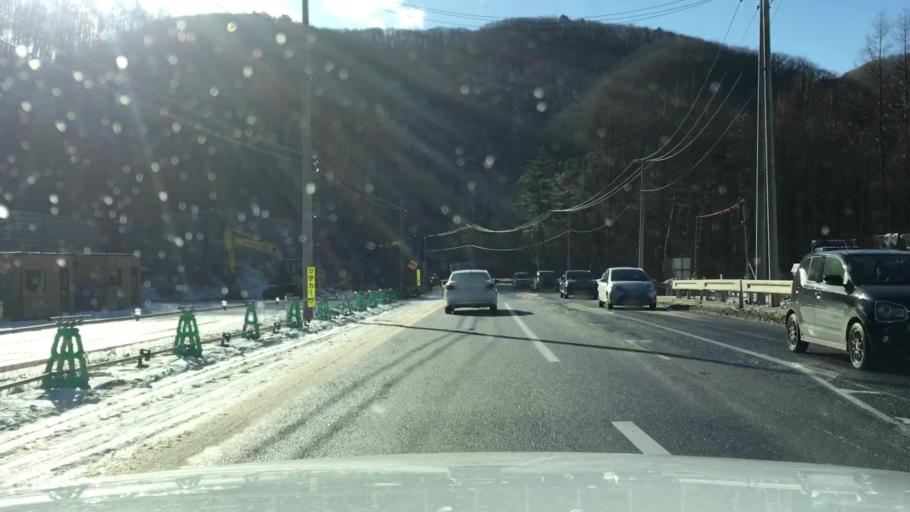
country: JP
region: Iwate
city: Morioka-shi
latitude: 39.6294
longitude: 141.4612
